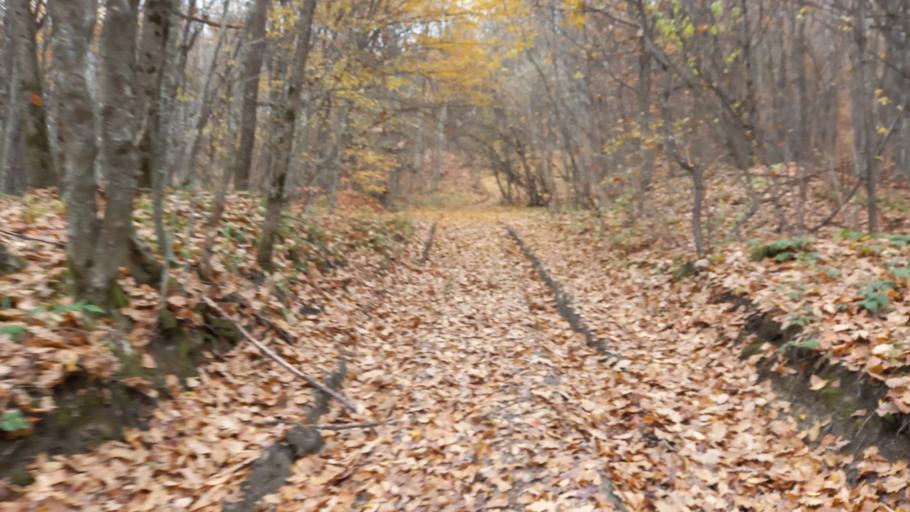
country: RU
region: Krasnodarskiy
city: Goryachiy Klyuch
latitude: 44.4954
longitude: 39.2755
